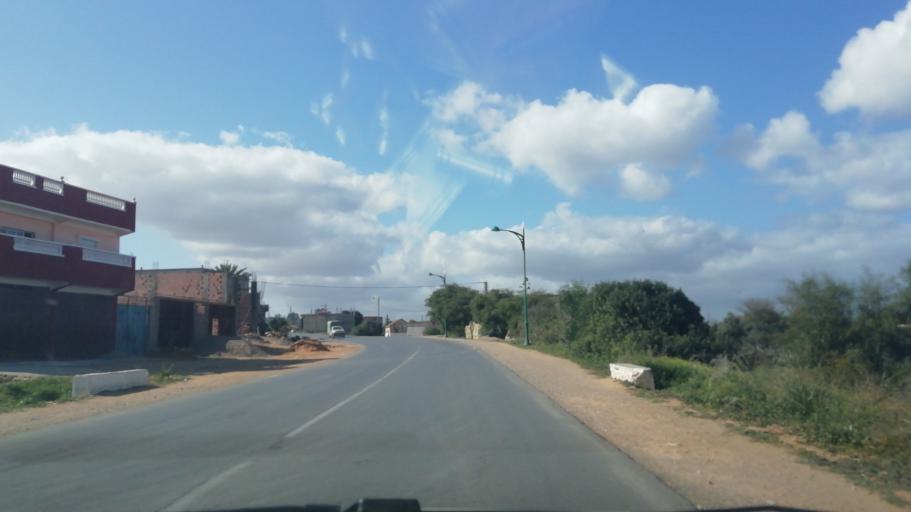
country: DZ
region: Relizane
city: Mazouna
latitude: 36.2796
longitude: 0.6384
